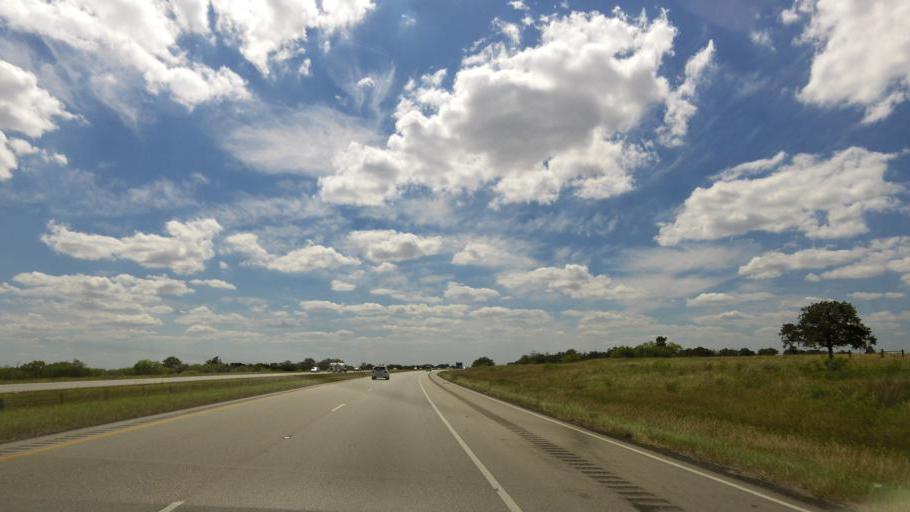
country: US
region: Texas
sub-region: Fayette County
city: Flatonia
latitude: 29.6923
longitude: -97.1621
